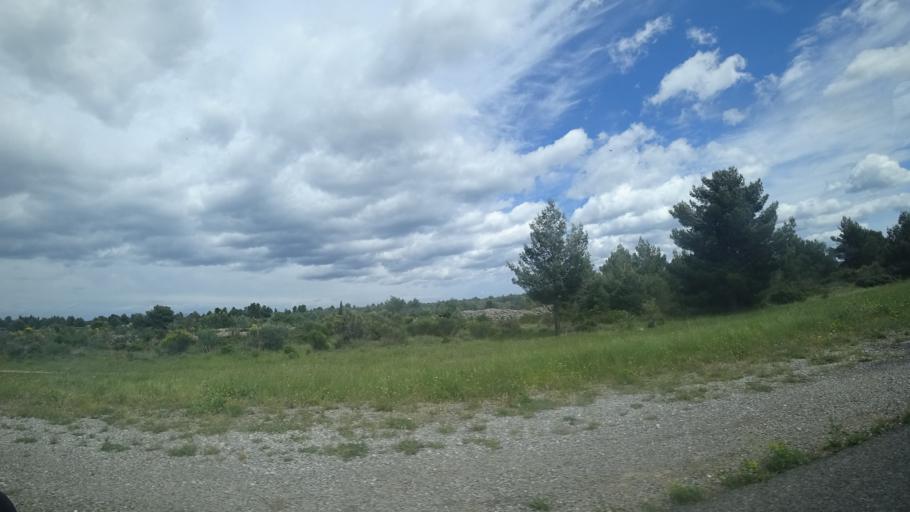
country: FR
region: Languedoc-Roussillon
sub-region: Departement de l'Aude
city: Leucate
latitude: 42.9221
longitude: 3.0176
